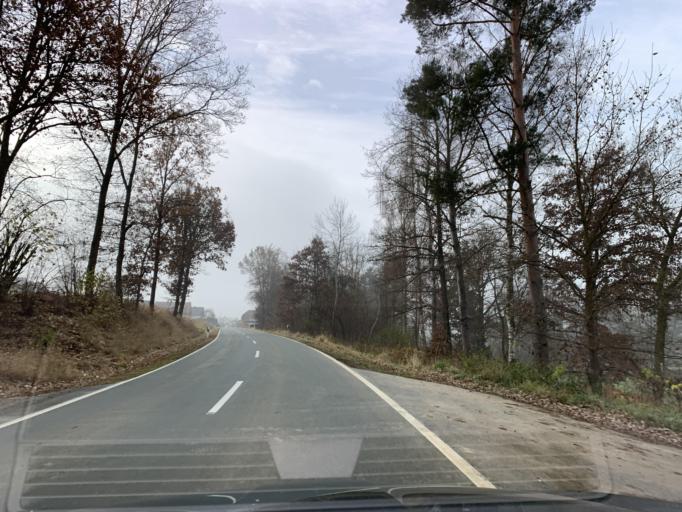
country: DE
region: Bavaria
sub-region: Upper Palatinate
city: Neunburg vorm Wald
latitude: 49.3658
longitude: 12.4009
